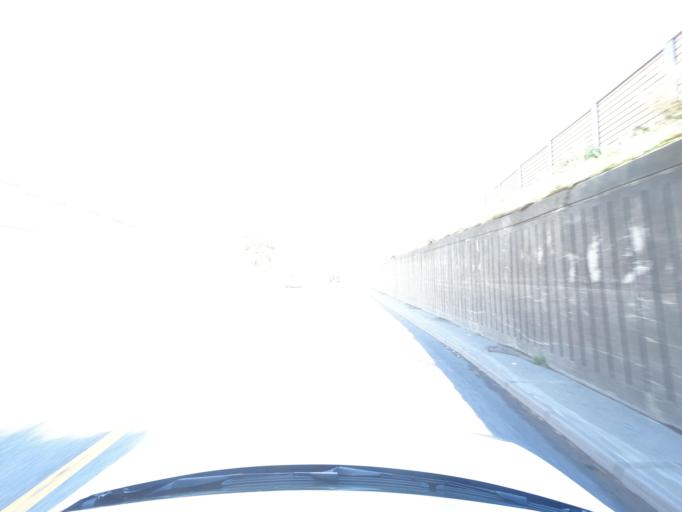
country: NO
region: Vestfold
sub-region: Horten
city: Horten
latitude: 59.4030
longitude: 10.4801
